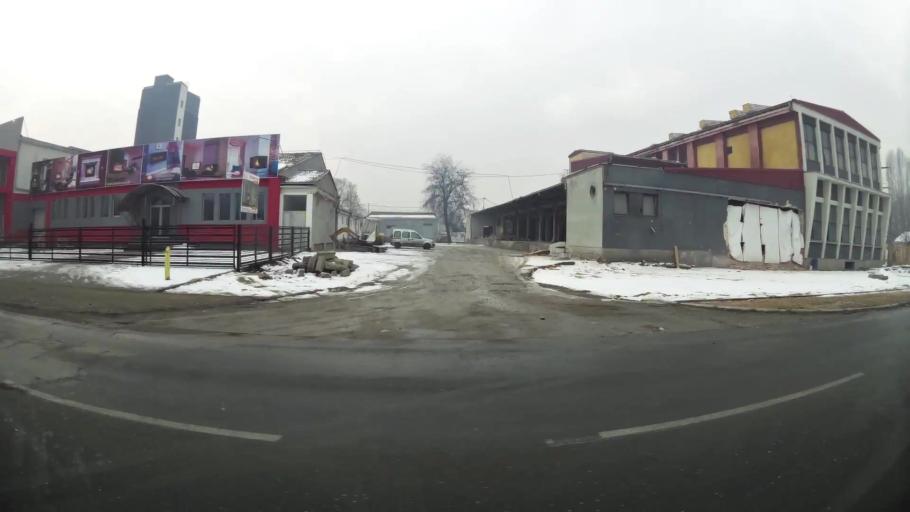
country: MK
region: Cair
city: Cair
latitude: 41.9992
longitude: 21.4609
